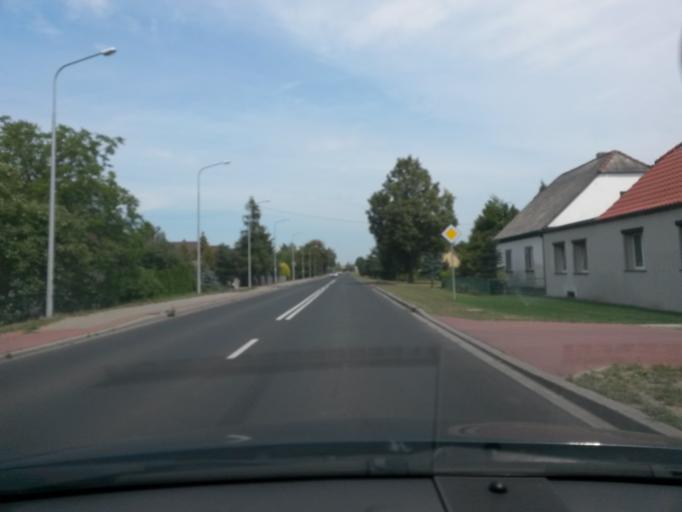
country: PL
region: Greater Poland Voivodeship
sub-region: Powiat sremski
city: Dolsk
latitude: 51.9575
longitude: 17.0708
